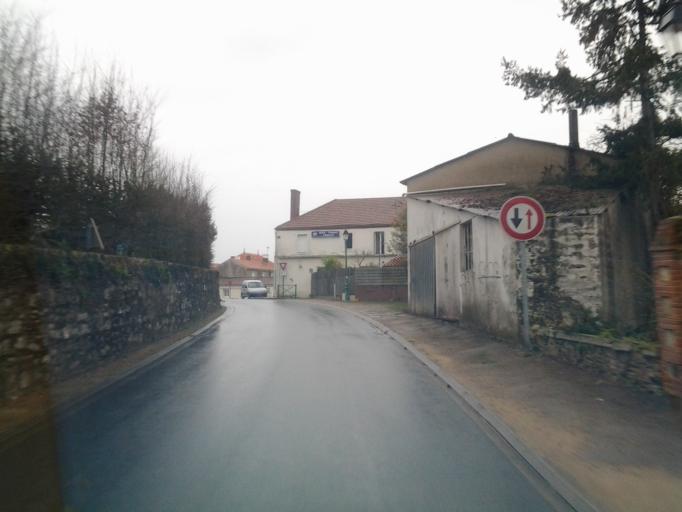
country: FR
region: Pays de la Loire
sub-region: Departement de la Vendee
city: Landeronde
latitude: 46.6596
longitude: -1.5727
